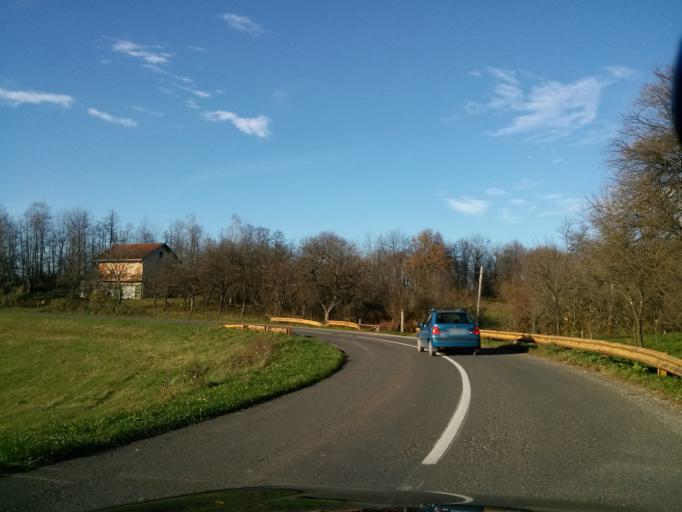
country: HR
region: Sisacko-Moslavacka
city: Gvozd
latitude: 45.3563
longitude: 15.9078
